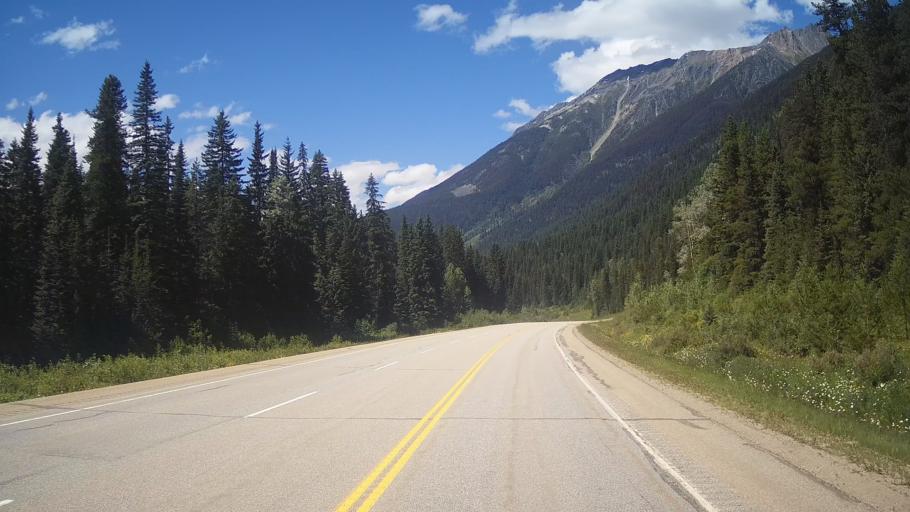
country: CA
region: Alberta
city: Grande Cache
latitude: 53.0102
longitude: -119.0651
